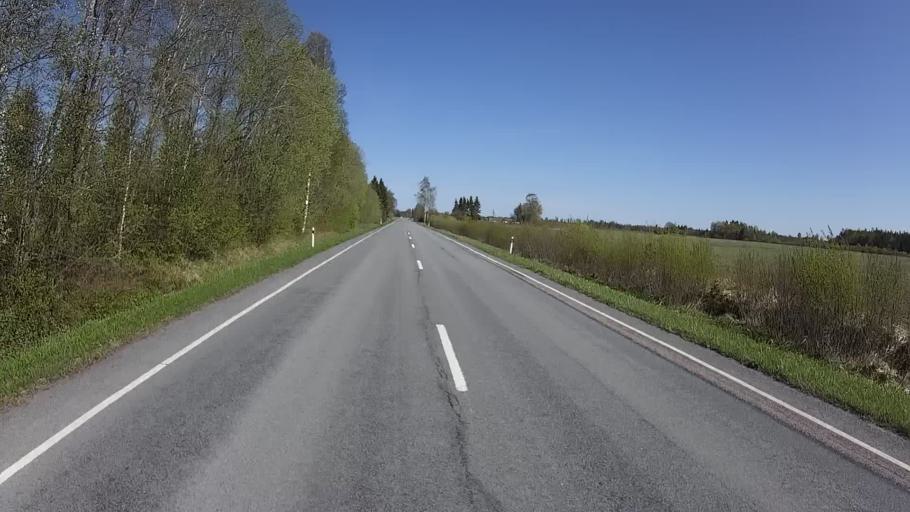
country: EE
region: Raplamaa
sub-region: Jaervakandi vald
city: Jarvakandi
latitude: 58.8323
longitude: 24.7972
